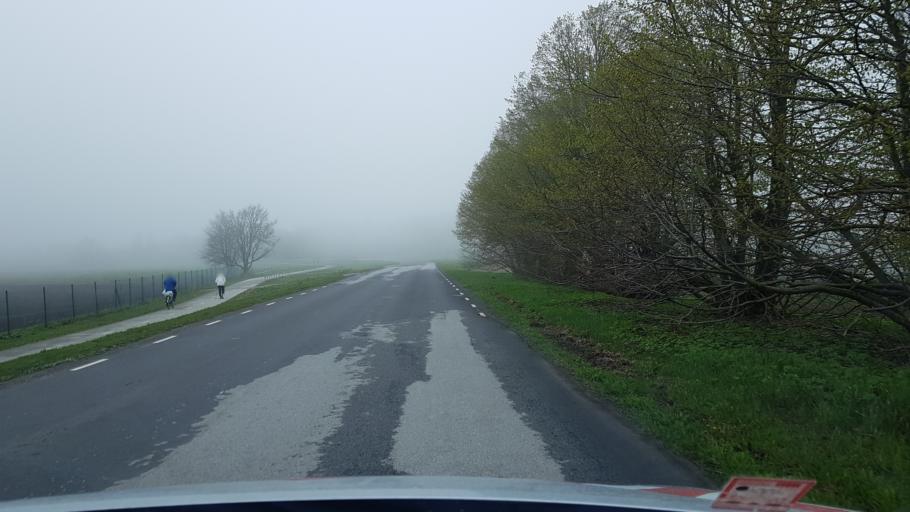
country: EE
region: Harju
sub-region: Joelaehtme vald
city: Loo
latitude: 59.4249
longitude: 24.9445
